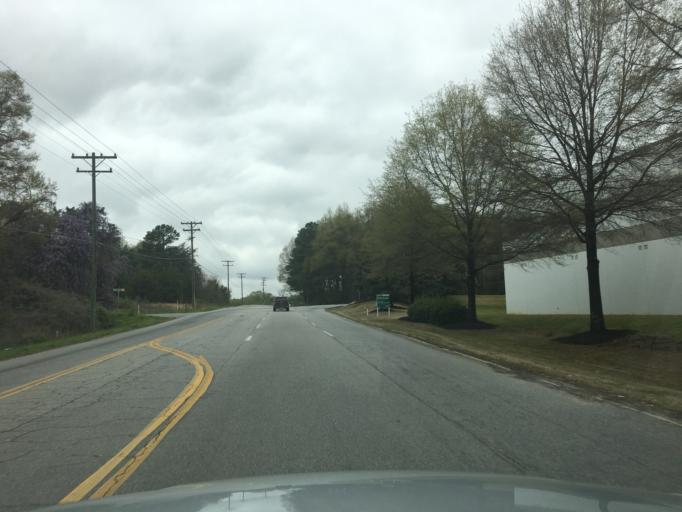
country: US
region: South Carolina
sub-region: Spartanburg County
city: Fairforest
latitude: 34.9683
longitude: -82.0303
